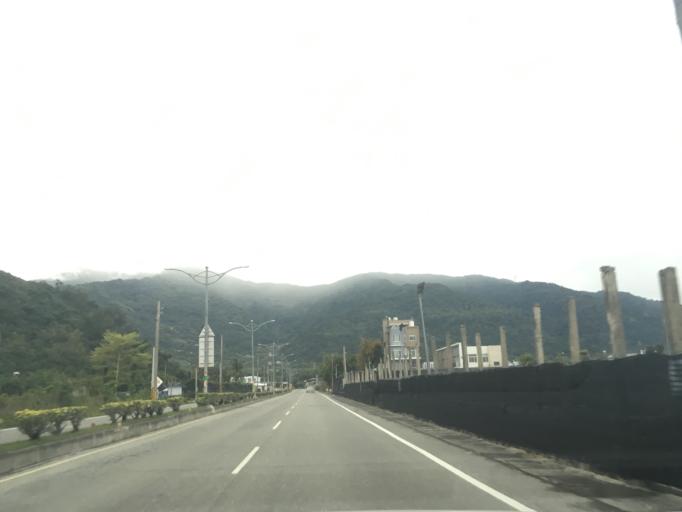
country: TW
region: Taiwan
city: Taitung City
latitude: 22.6964
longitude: 121.0441
